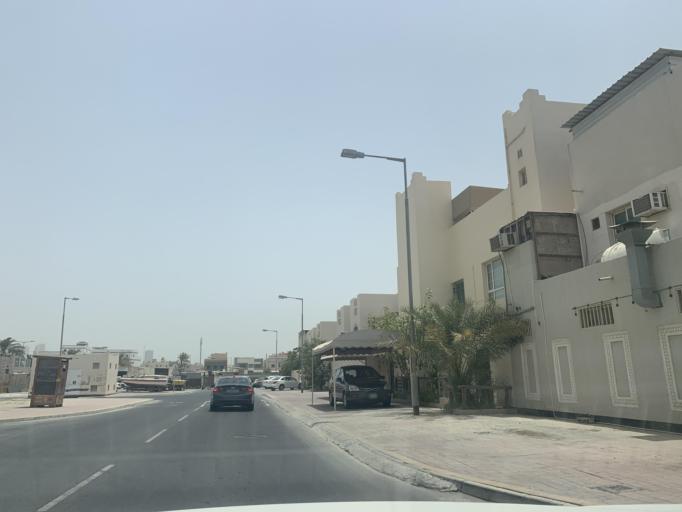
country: BH
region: Manama
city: Jidd Hafs
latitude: 26.2130
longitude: 50.5365
